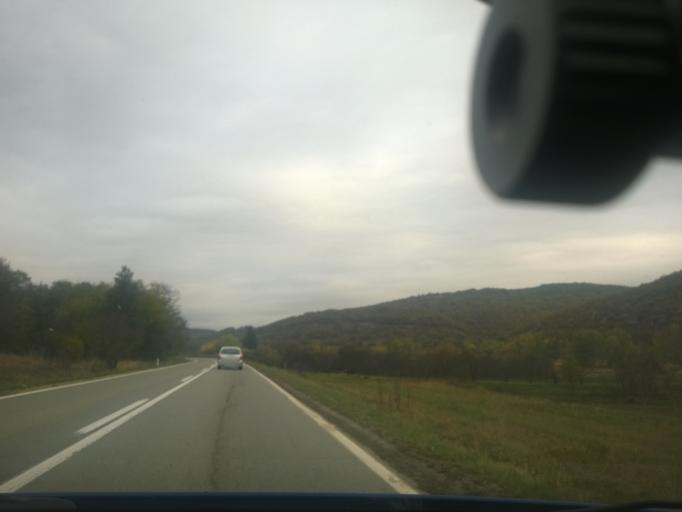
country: RS
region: Central Serbia
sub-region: Pirotski Okrug
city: Dimitrovgrad
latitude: 43.0314
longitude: 22.7200
